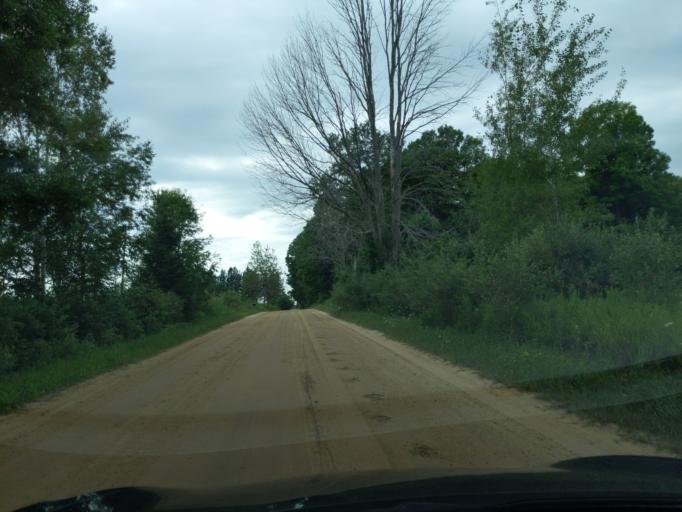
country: US
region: Michigan
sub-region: Clare County
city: Harrison
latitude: 44.0025
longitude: -84.9791
